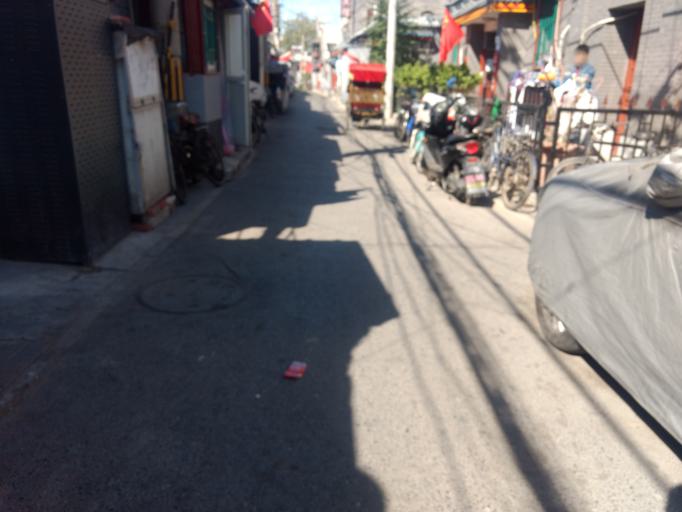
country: CN
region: Beijing
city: Beijing
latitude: 39.8912
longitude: 116.3836
